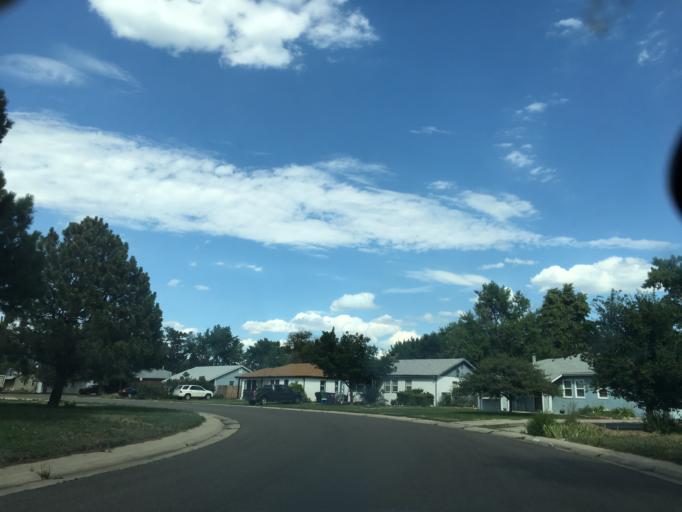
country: US
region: Colorado
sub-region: Arapahoe County
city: Sheridan
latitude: 39.6883
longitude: -105.0389
